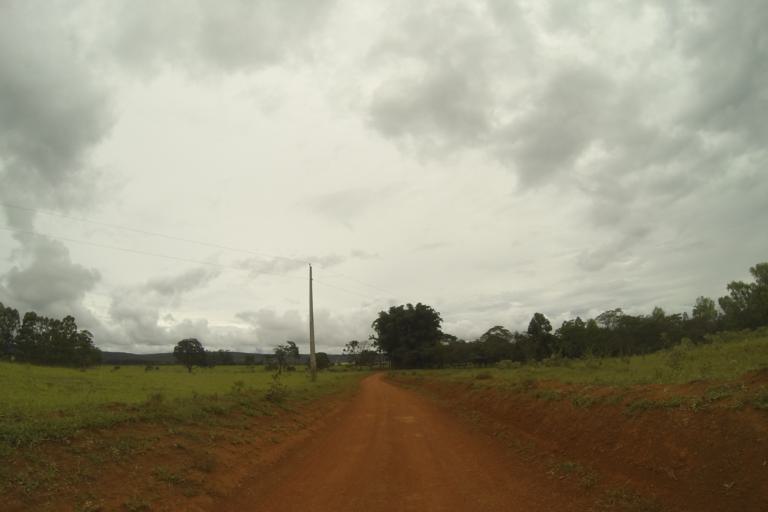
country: BR
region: Minas Gerais
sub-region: Ibia
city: Ibia
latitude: -19.7332
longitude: -46.6061
